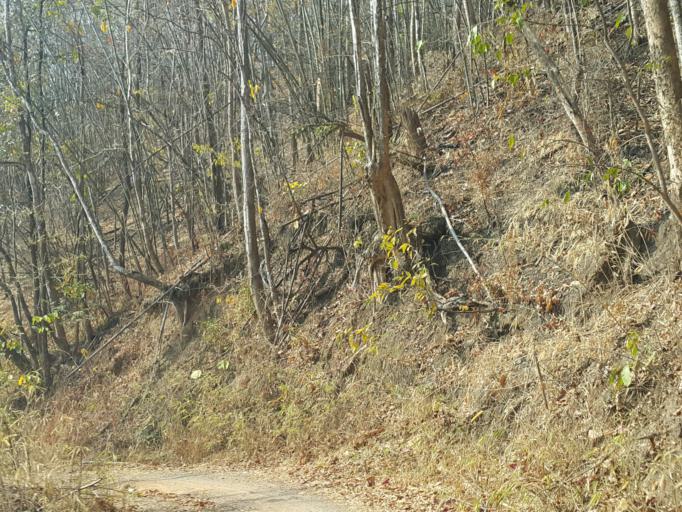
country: TH
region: Chiang Mai
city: Hang Dong
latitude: 18.7504
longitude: 98.8576
